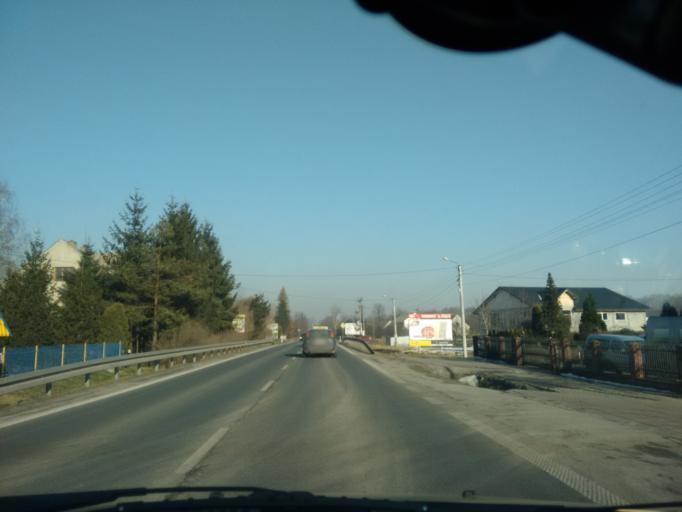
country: PL
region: Lesser Poland Voivodeship
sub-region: Powiat wadowicki
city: Chocznia
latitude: 49.8761
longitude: 19.4574
